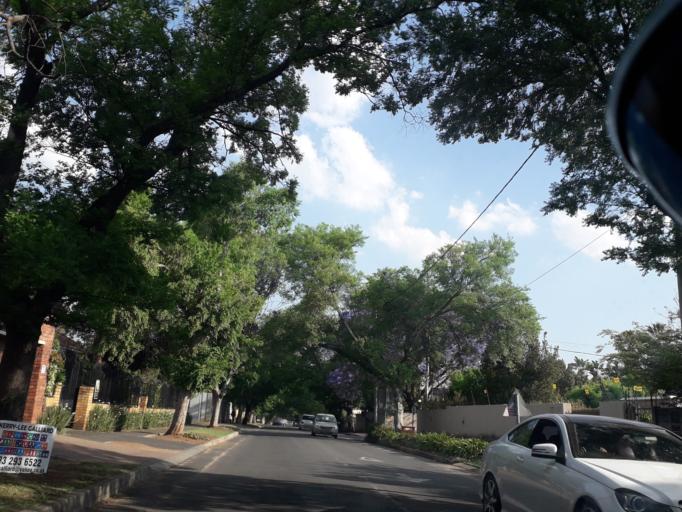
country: ZA
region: Gauteng
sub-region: City of Johannesburg Metropolitan Municipality
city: Johannesburg
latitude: -26.1422
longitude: 28.0801
